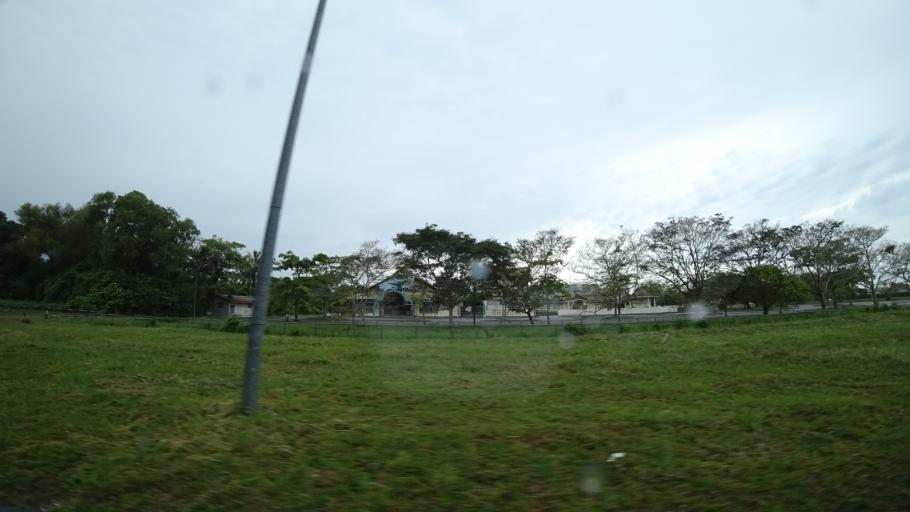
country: BN
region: Belait
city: Seria
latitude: 4.6057
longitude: 114.3290
